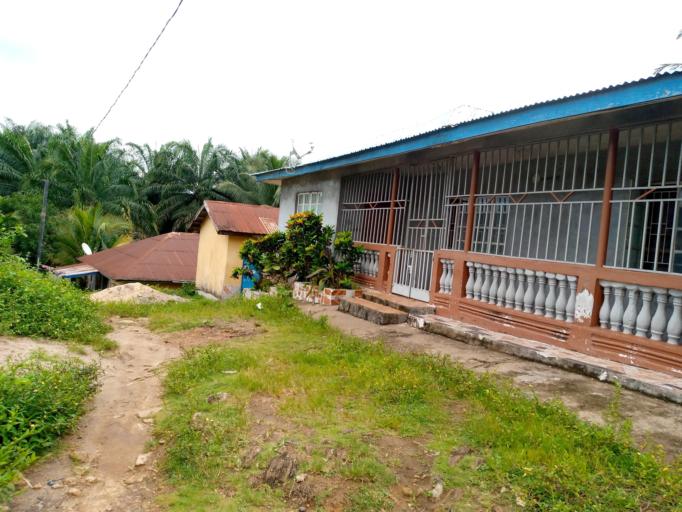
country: SL
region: Northern Province
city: Magburaka
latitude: 8.7264
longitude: -11.9495
